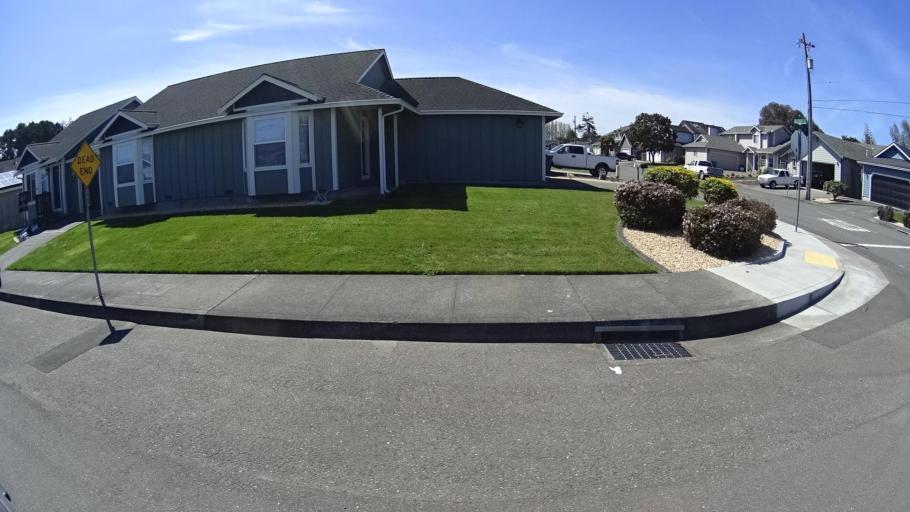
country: US
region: California
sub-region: Humboldt County
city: Myrtletown
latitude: 40.7878
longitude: -124.1260
